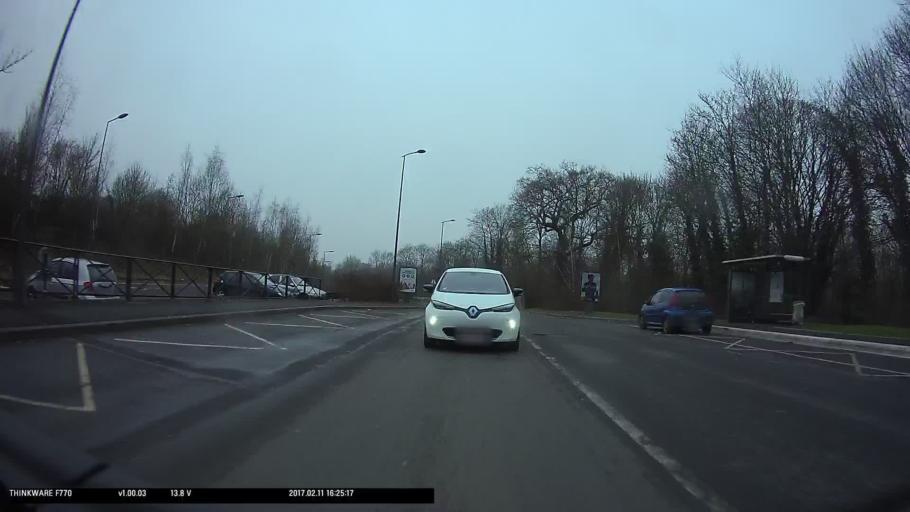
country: FR
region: Ile-de-France
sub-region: Departement du Val-d'Oise
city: Osny
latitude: 49.0637
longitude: 2.0565
